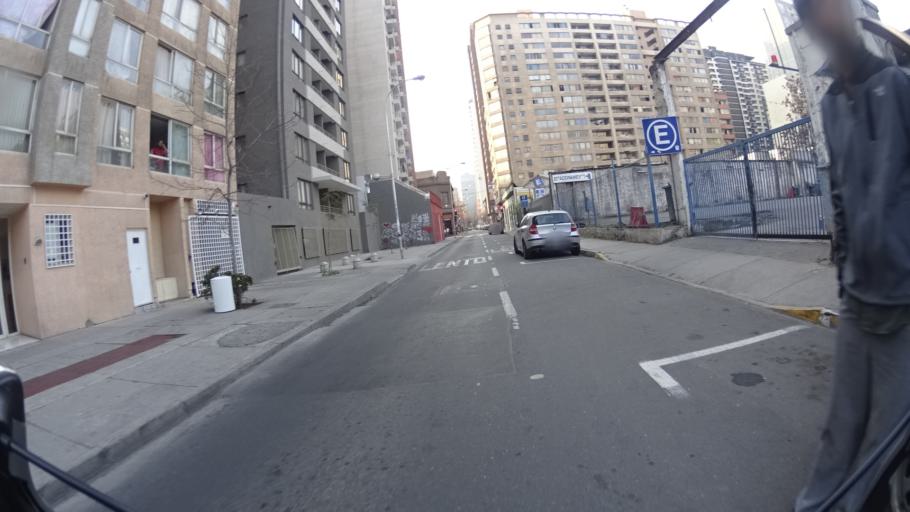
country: CL
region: Santiago Metropolitan
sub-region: Provincia de Santiago
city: Santiago
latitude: -33.4495
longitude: -70.6484
